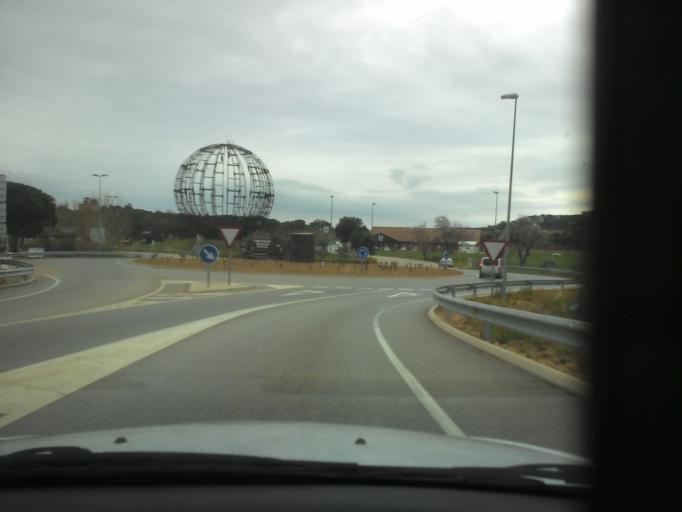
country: ES
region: Catalonia
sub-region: Provincia de Girona
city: Calonge
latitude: 41.8557
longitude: 3.0794
